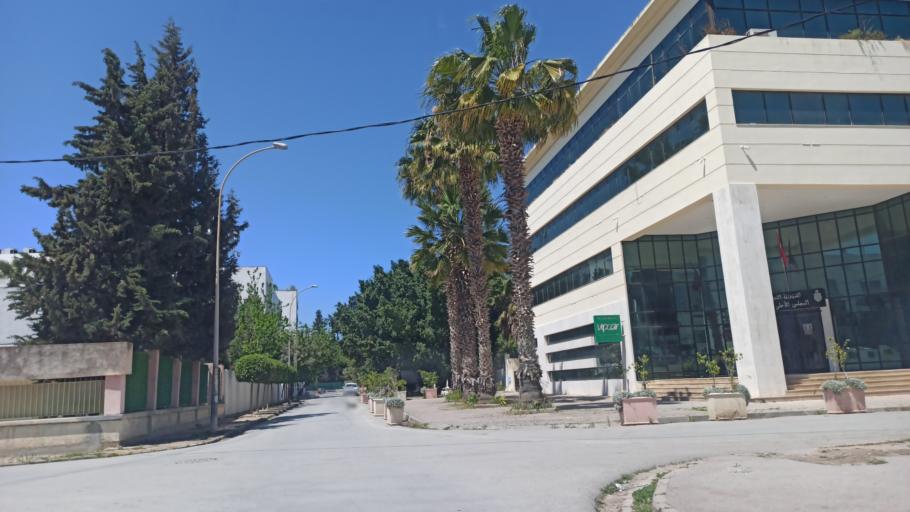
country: TN
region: Tunis
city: Tunis
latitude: 36.8245
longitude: 10.1836
